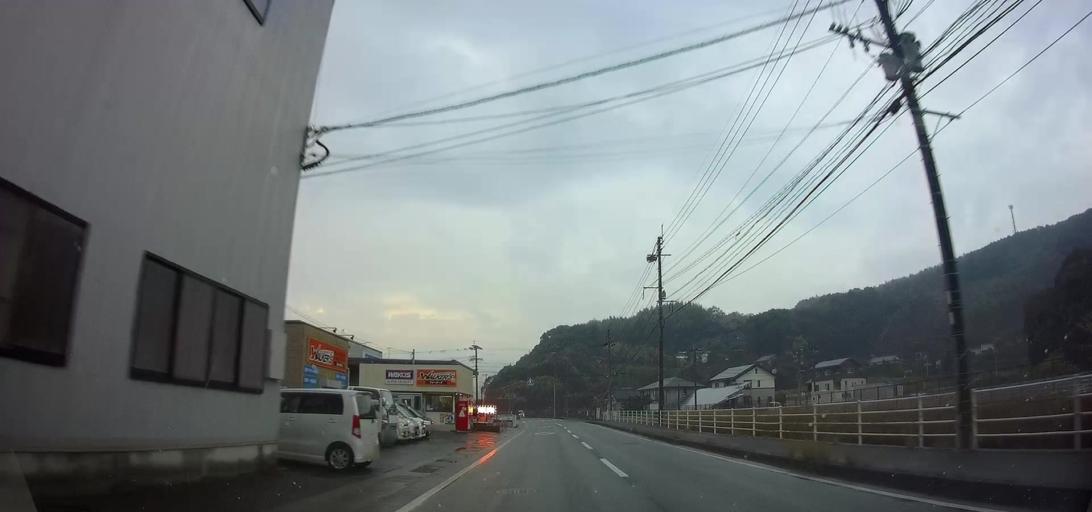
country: JP
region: Nagasaki
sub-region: Isahaya-shi
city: Isahaya
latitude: 32.8490
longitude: 130.0048
